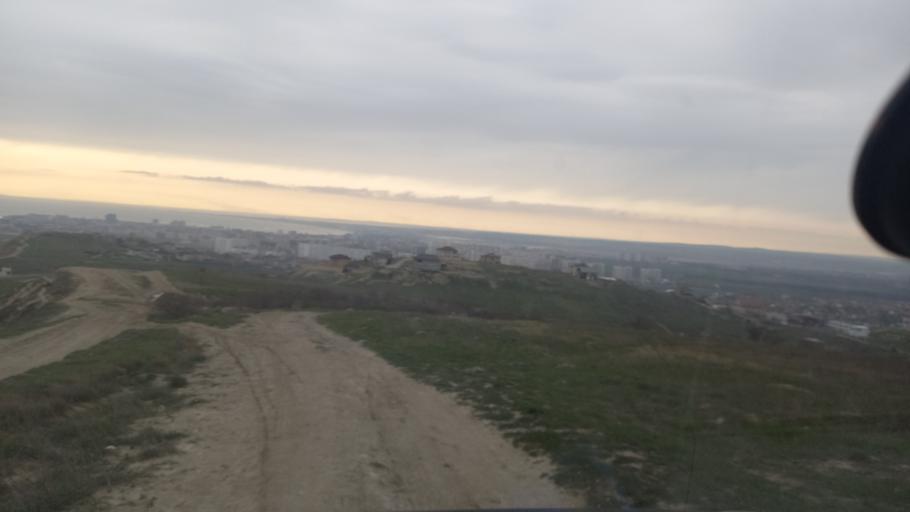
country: RU
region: Krasnodarskiy
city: Anapa
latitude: 44.8505
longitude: 37.3430
